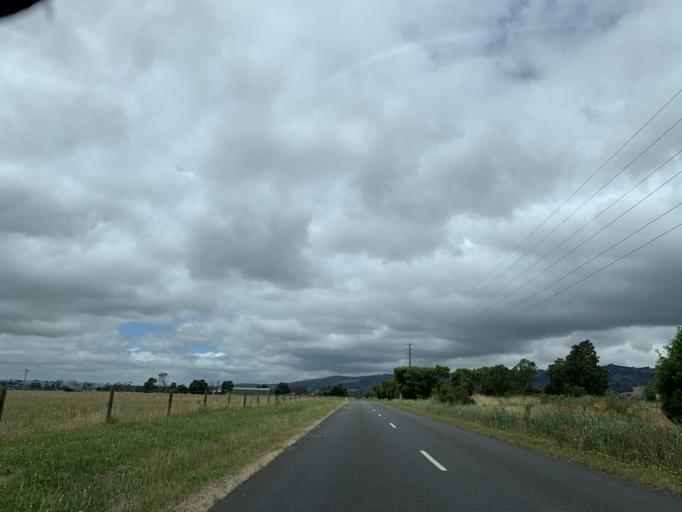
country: AU
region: Victoria
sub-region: Latrobe
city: Moe
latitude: -38.2081
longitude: 146.1270
